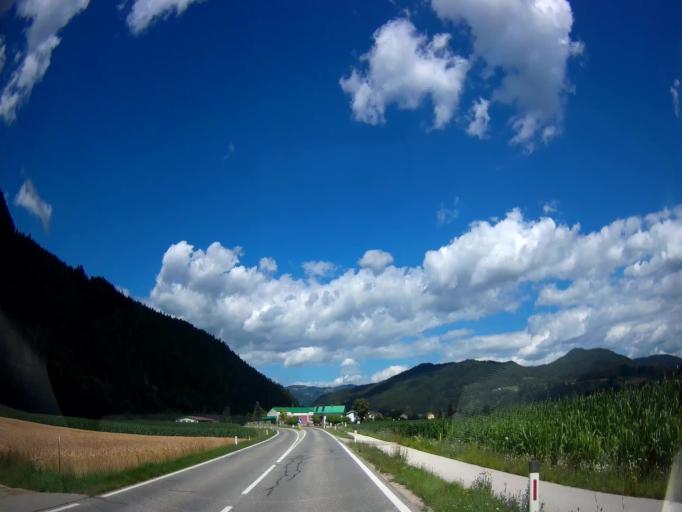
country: AT
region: Carinthia
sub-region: Politischer Bezirk Klagenfurt Land
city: Poggersdorf
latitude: 46.6795
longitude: 14.4812
